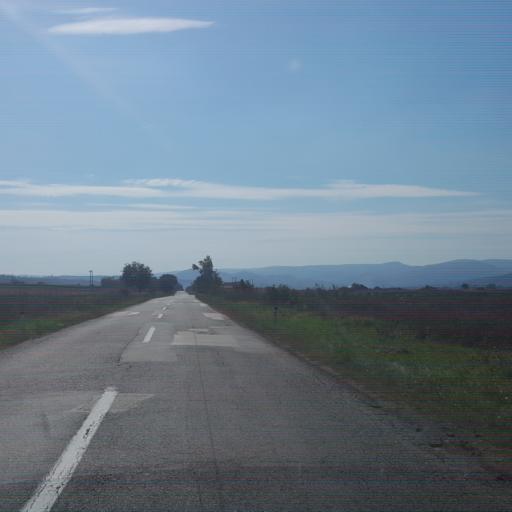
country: RS
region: Central Serbia
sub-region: Zajecarski Okrug
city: Knjazevac
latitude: 43.6071
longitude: 22.2783
